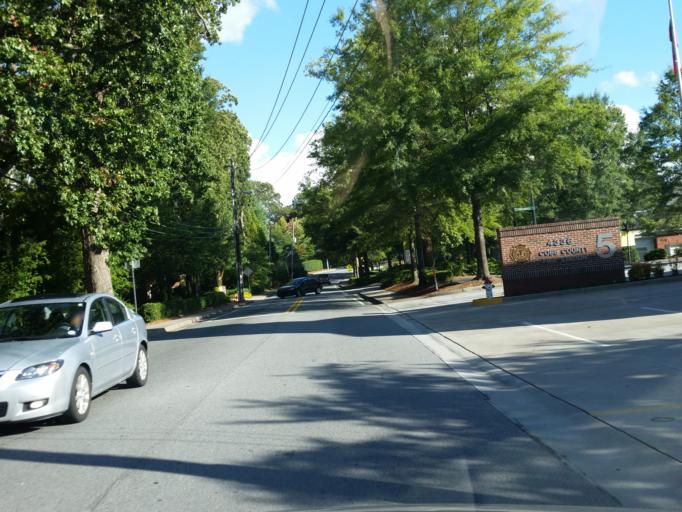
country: US
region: Georgia
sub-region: Cobb County
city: Vinings
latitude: 33.8661
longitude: -84.4659
